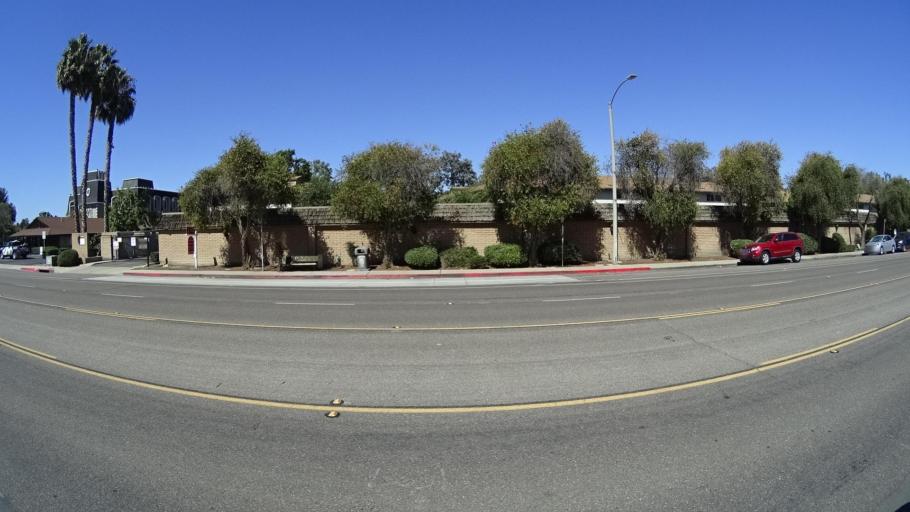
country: US
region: California
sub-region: San Diego County
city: Bonita
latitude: 32.6589
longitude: -117.0391
